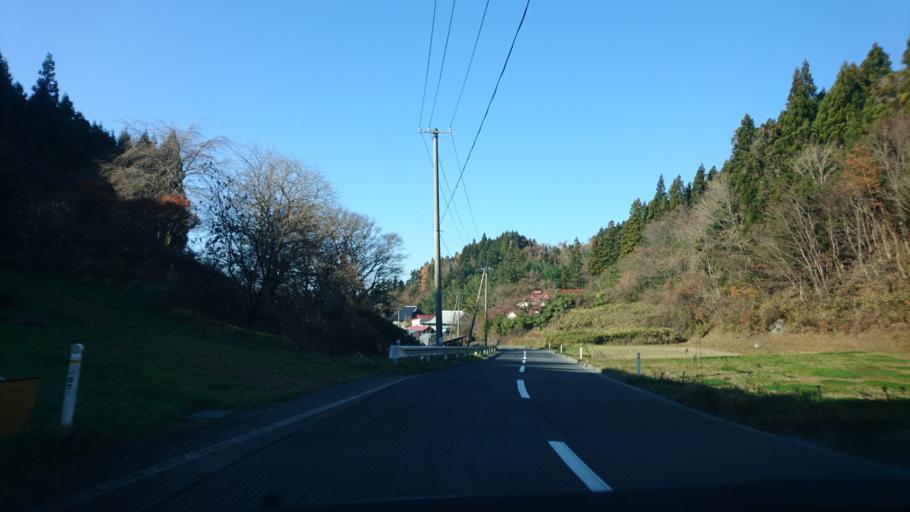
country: JP
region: Iwate
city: Ichinoseki
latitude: 38.9006
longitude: 141.4069
